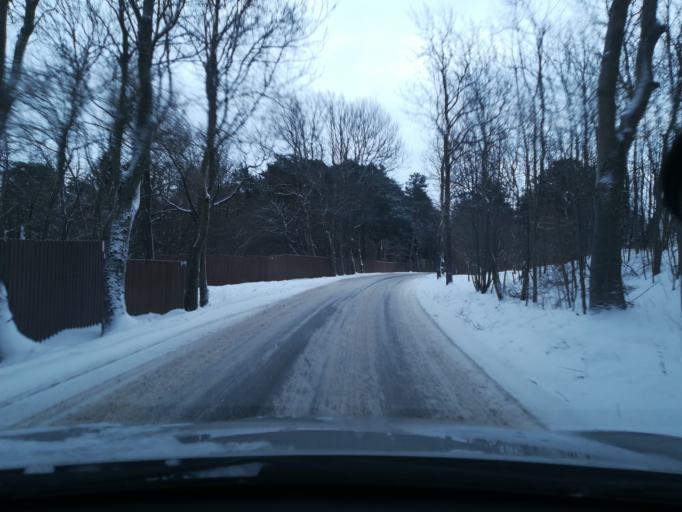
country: EE
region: Harju
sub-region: Harku vald
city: Tabasalu
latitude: 59.4474
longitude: 24.4926
